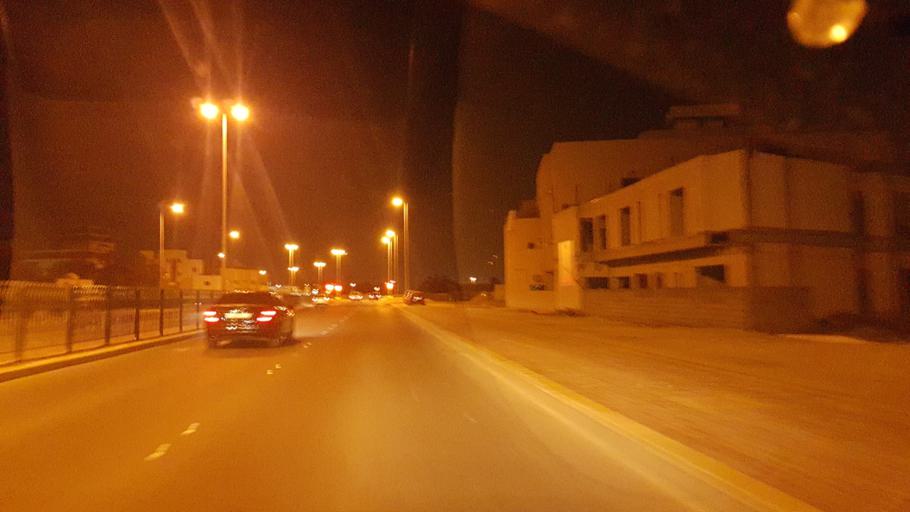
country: BH
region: Muharraq
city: Al Hadd
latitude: 26.2522
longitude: 50.6510
